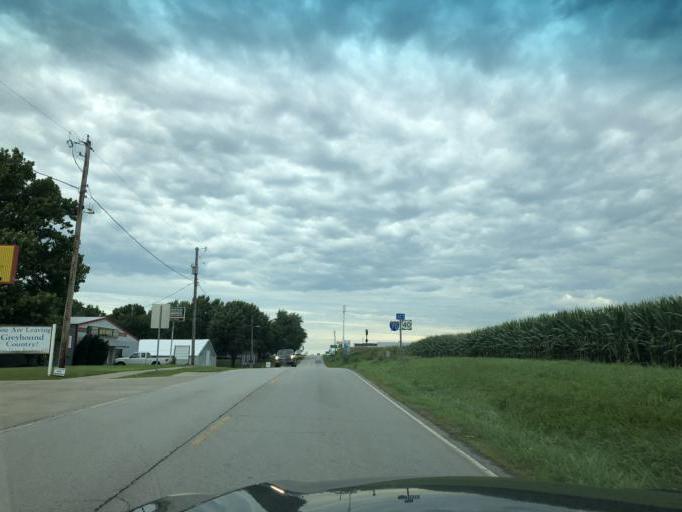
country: US
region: Missouri
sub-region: Saline County
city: Sweet Springs
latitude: 38.9732
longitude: -93.4152
